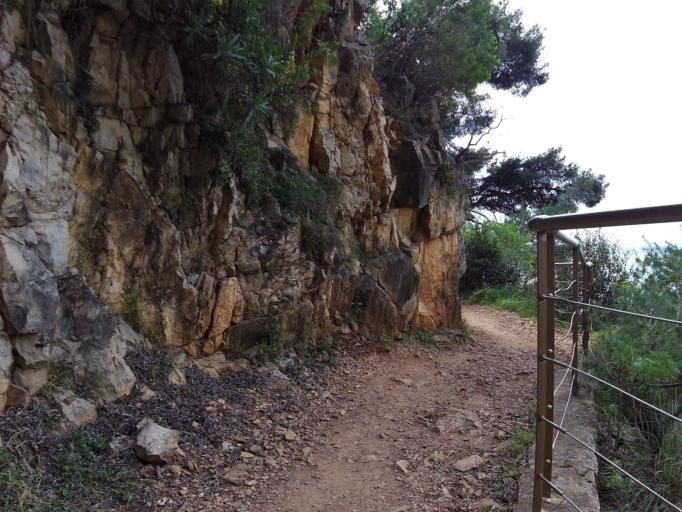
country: FR
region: Provence-Alpes-Cote d'Azur
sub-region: Departement des Alpes-Maritimes
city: Saint-Jean-Cap-Ferrat
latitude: 43.6834
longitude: 7.3247
